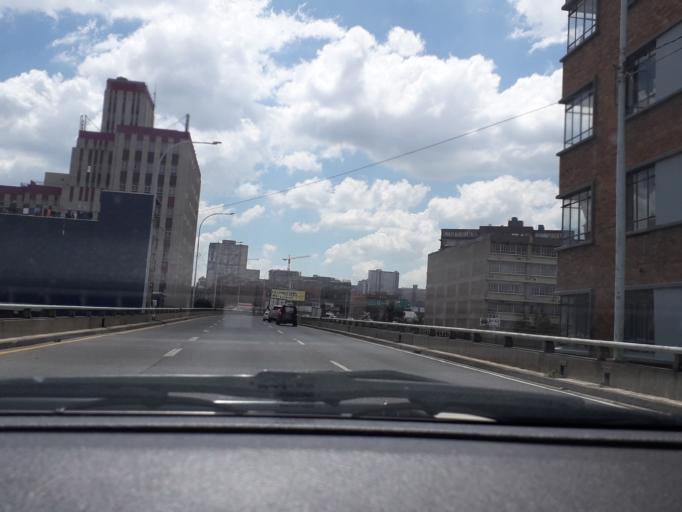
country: ZA
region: Gauteng
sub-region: City of Johannesburg Metropolitan Municipality
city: Johannesburg
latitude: -26.2058
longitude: 28.0545
